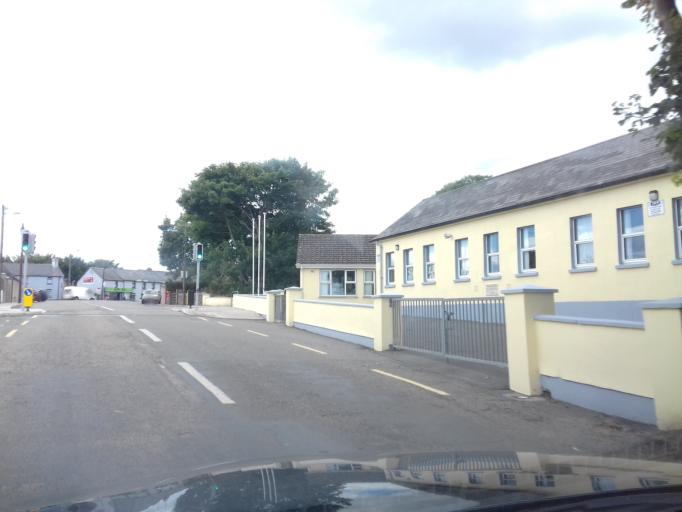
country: IE
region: Munster
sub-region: Waterford
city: Portlaw
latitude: 52.1767
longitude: -7.3340
